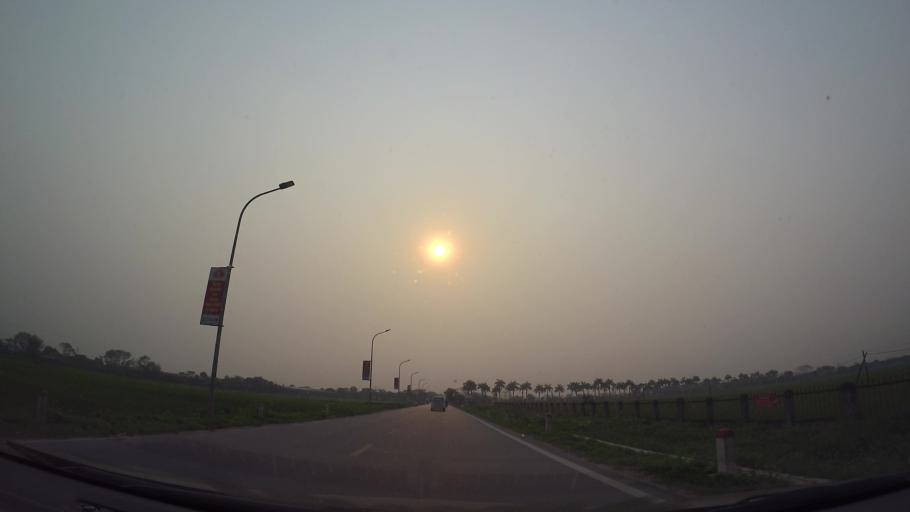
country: VN
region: Ha Noi
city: Thuong Tin
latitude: 20.8692
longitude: 105.8374
